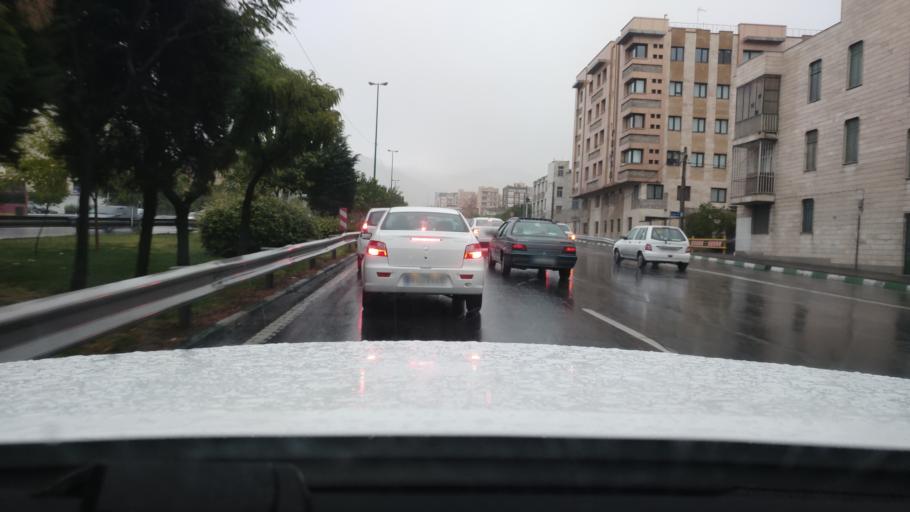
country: IR
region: Tehran
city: Tehran
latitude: 35.7289
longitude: 51.3105
